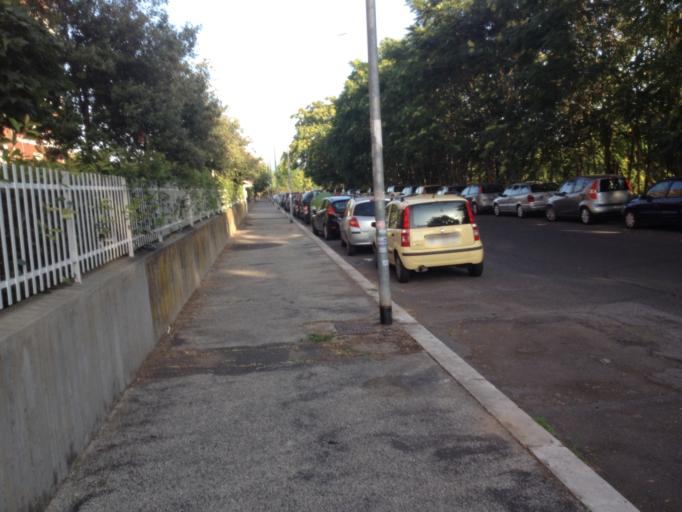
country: IT
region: Latium
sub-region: Citta metropolitana di Roma Capitale
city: Rome
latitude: 41.8654
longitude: 12.5764
